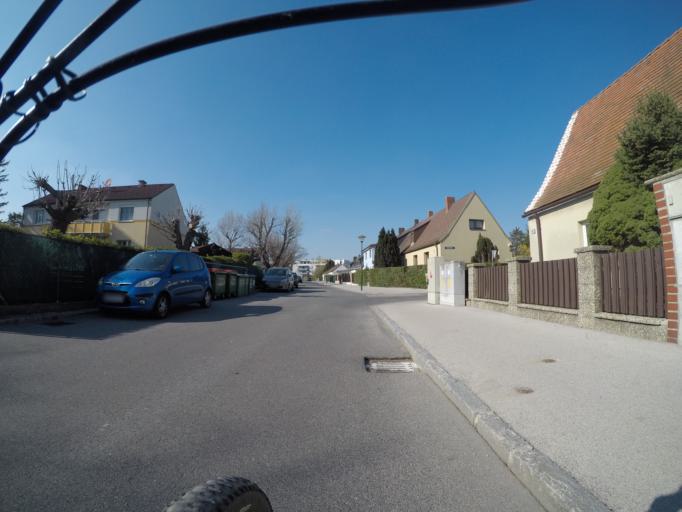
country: AT
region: Lower Austria
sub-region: Politischer Bezirk Modling
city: Neu-Guntramsdorf
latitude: 48.0645
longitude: 16.3219
